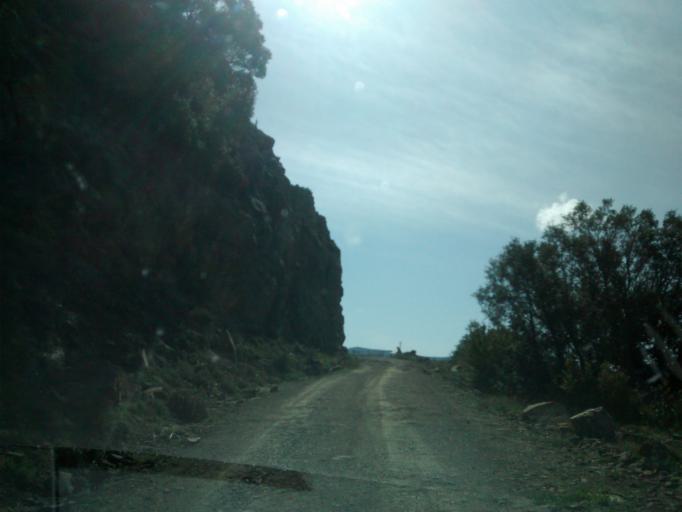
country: ES
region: Aragon
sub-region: Provincia de Huesca
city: Arguis
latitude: 42.3261
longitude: -0.3946
